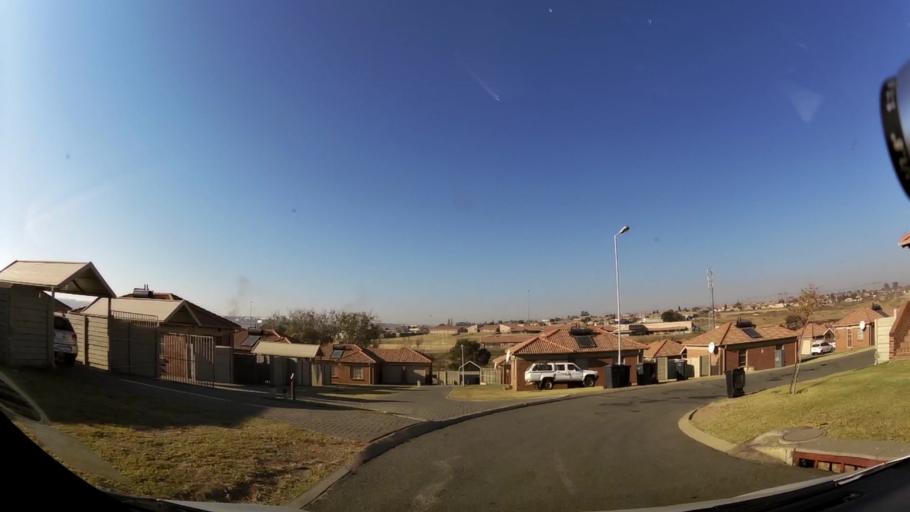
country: ZA
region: Gauteng
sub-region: City of Johannesburg Metropolitan Municipality
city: Midrand
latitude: -25.9099
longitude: 28.1103
